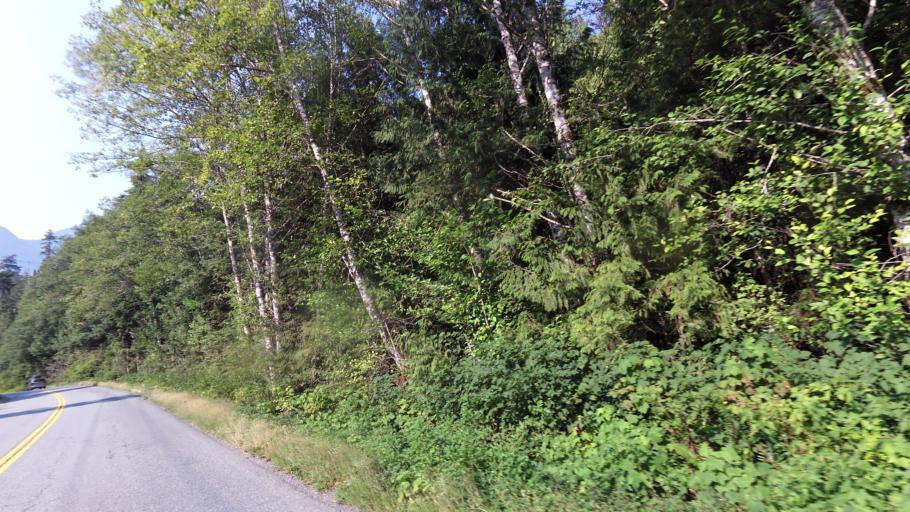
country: CA
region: British Columbia
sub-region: Regional District of Alberni-Clayoquot
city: Ucluelet
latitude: 49.1029
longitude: -125.4533
